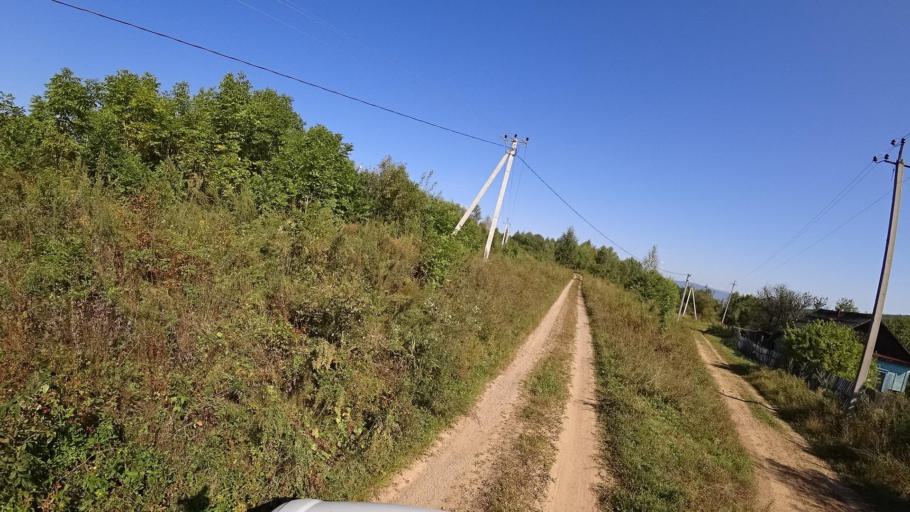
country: RU
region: Jewish Autonomous Oblast
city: Bira
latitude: 49.0099
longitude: 132.4695
